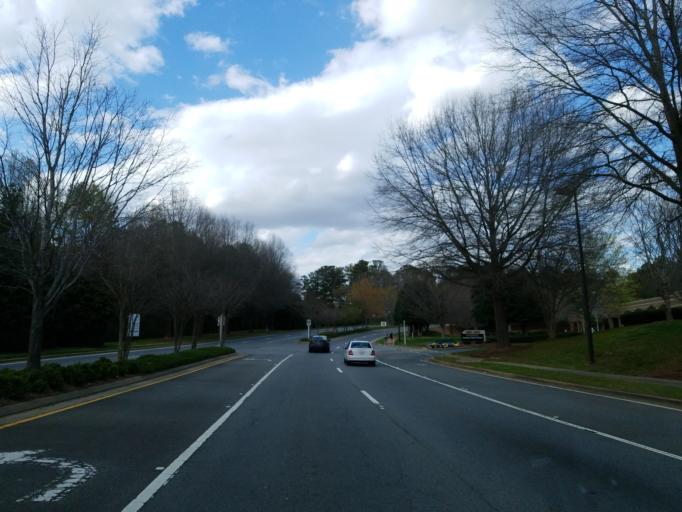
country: US
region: Georgia
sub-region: Cobb County
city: Kennesaw
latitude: 34.0325
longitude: -84.5558
